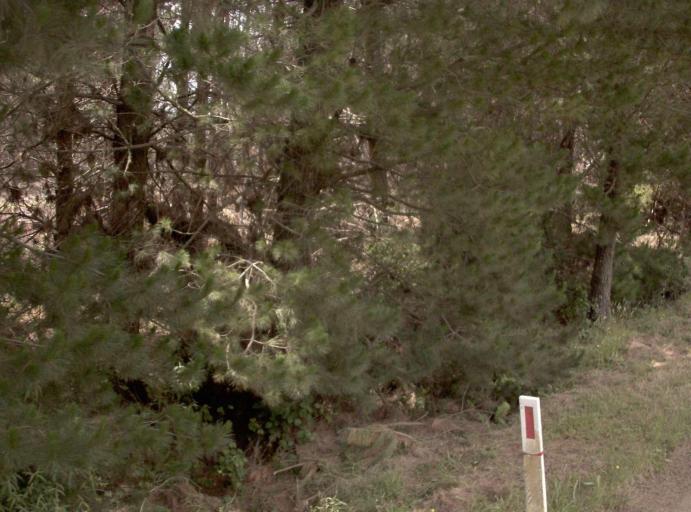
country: AU
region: Victoria
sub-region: Latrobe
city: Traralgon
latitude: -38.4136
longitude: 146.6186
